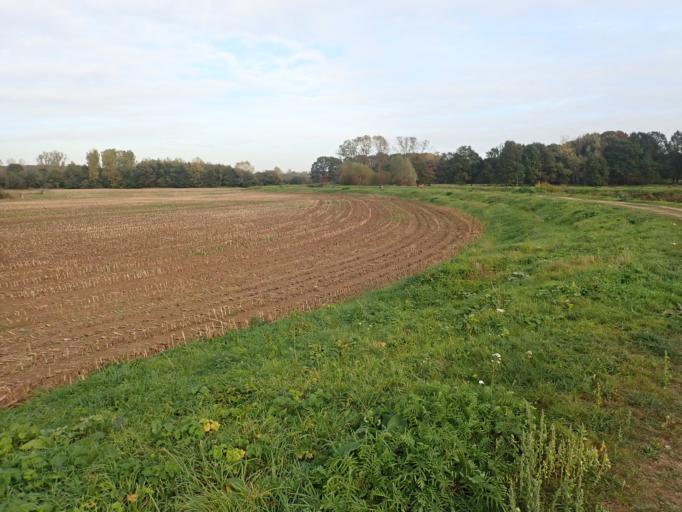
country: BE
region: Flanders
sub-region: Provincie Antwerpen
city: Berlaar
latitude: 51.1217
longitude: 4.6997
